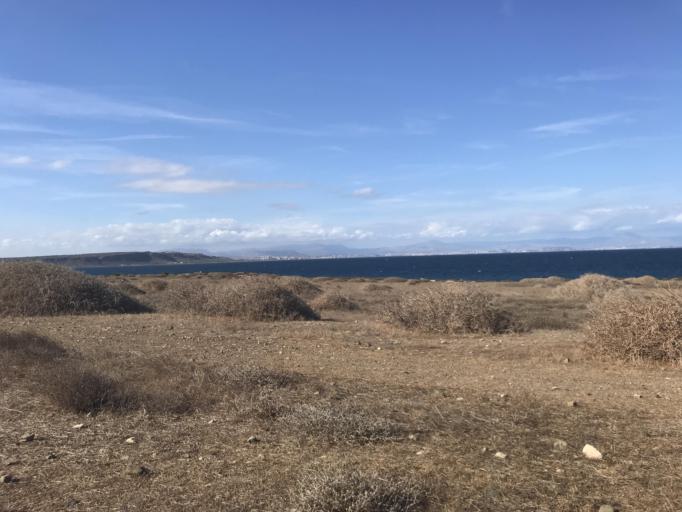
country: ES
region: Valencia
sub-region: Provincia de Alicante
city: Santa Pola
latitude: 38.1642
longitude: -0.4707
